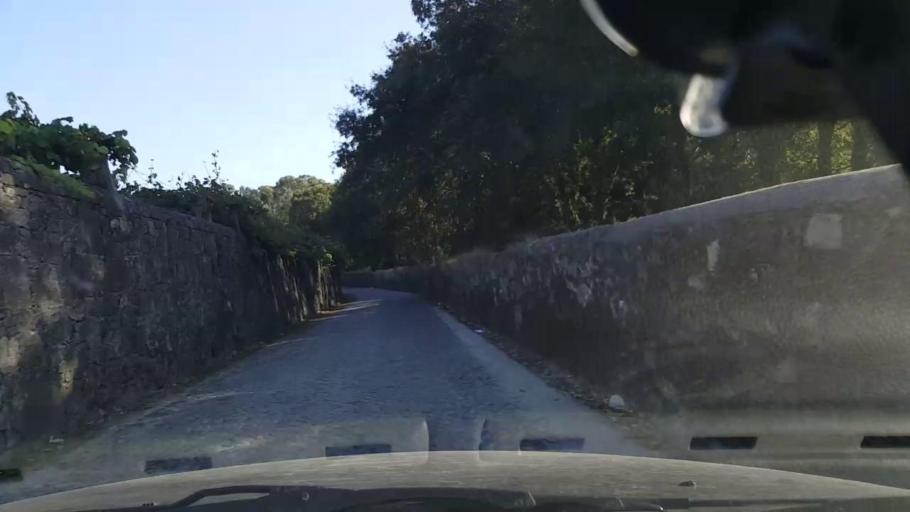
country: PT
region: Porto
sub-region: Vila do Conde
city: Arvore
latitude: 41.3419
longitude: -8.6866
